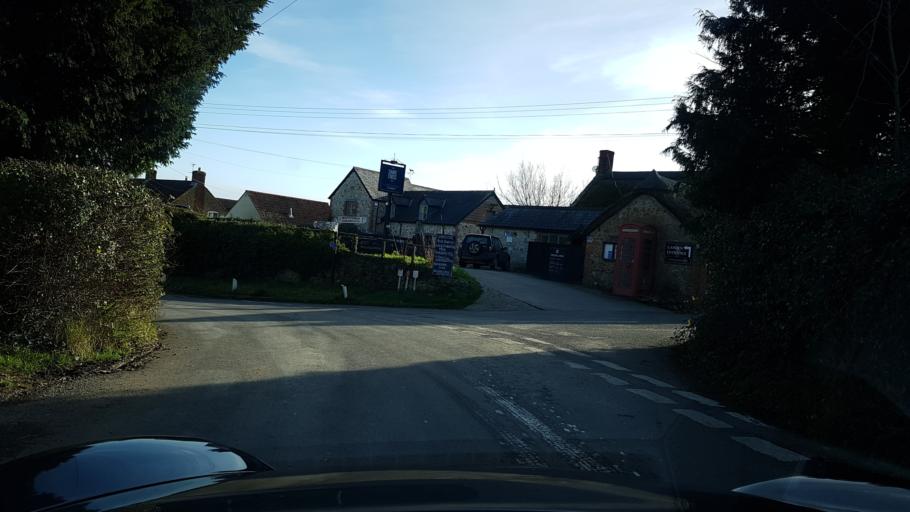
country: GB
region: England
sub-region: Dorset
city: Bridport
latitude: 50.7789
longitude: -2.8308
